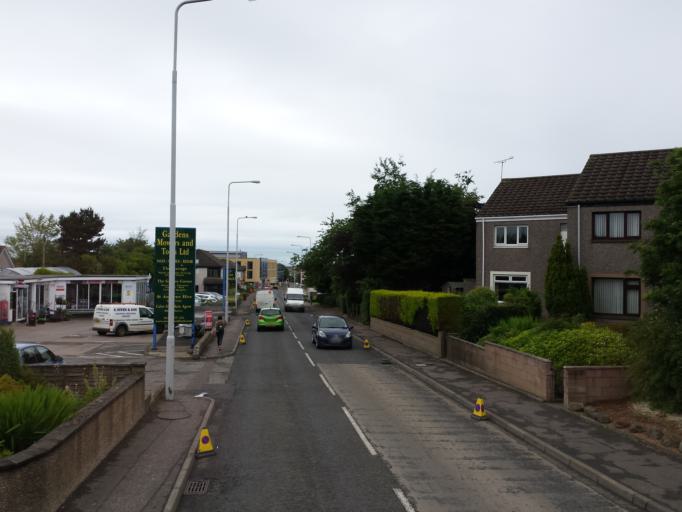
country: GB
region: Scotland
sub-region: Fife
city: Saint Andrews
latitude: 56.3293
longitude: -2.8058
